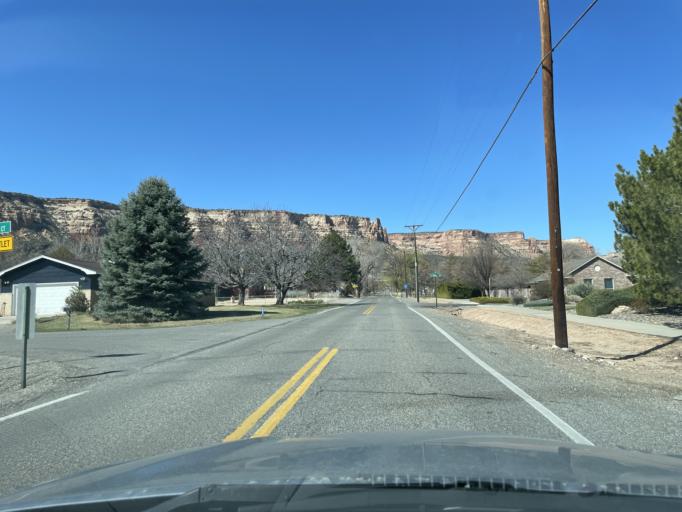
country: US
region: Colorado
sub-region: Mesa County
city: Redlands
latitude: 39.0850
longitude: -108.6710
